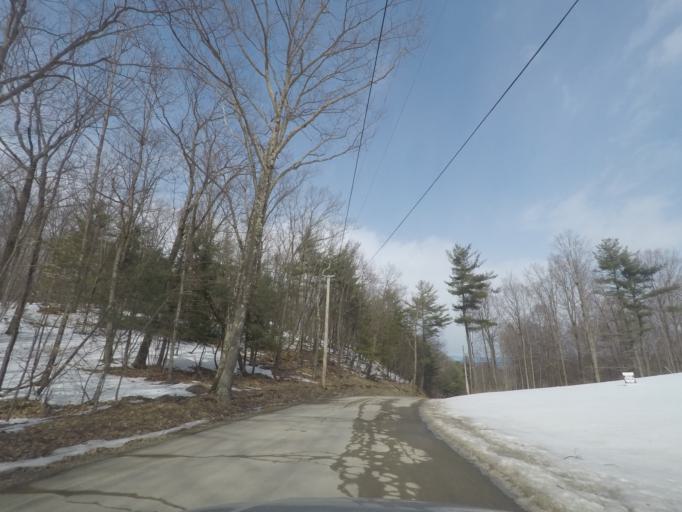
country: US
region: New York
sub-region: Saratoga County
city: Waterford
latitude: 42.7794
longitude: -73.5974
